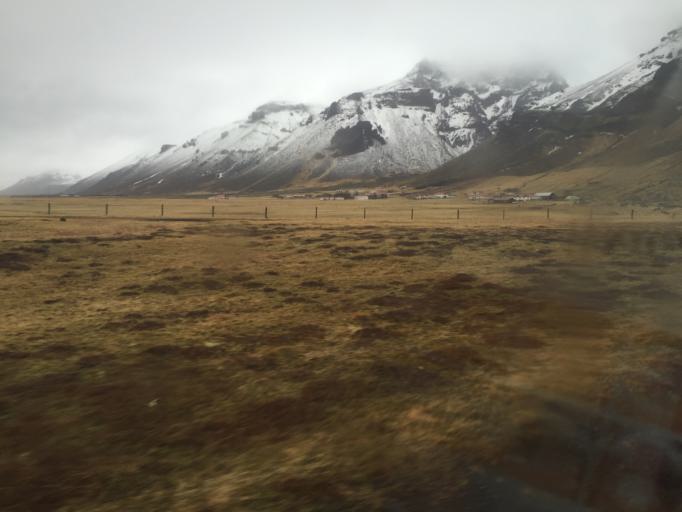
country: IS
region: East
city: Hoefn
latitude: 63.8989
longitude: -16.7034
